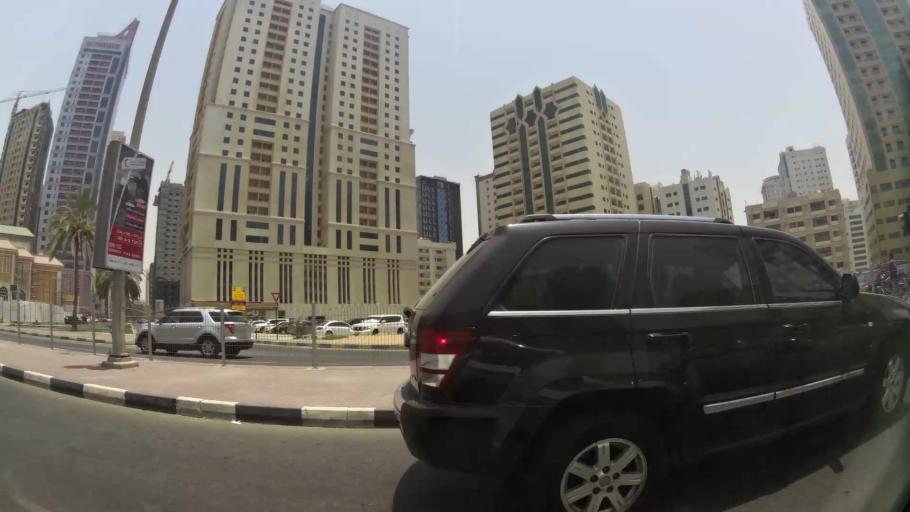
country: AE
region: Ash Shariqah
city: Sharjah
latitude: 25.3216
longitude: 55.3814
